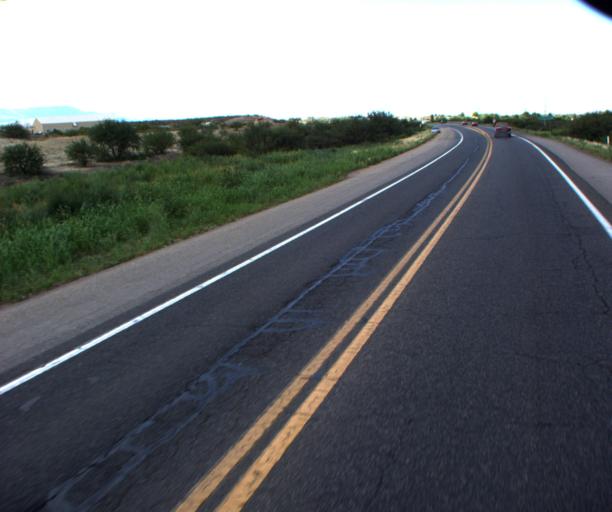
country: US
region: Arizona
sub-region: Yavapai County
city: Camp Verde
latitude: 34.5891
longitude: -111.8878
